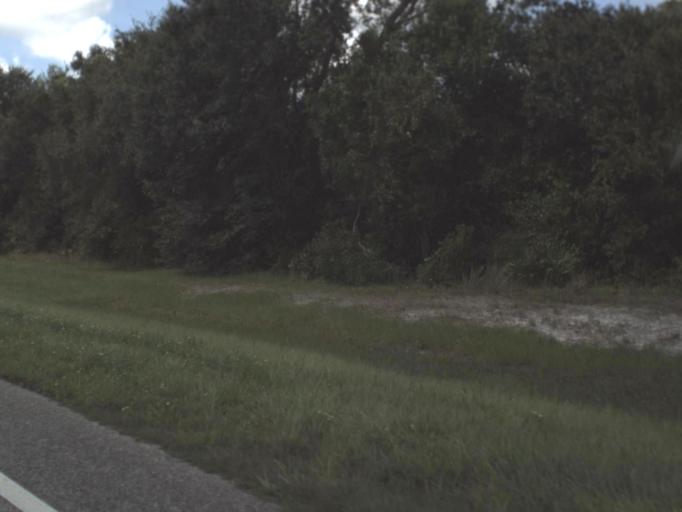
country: US
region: Florida
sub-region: DeSoto County
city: Arcadia
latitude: 27.2721
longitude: -81.8354
